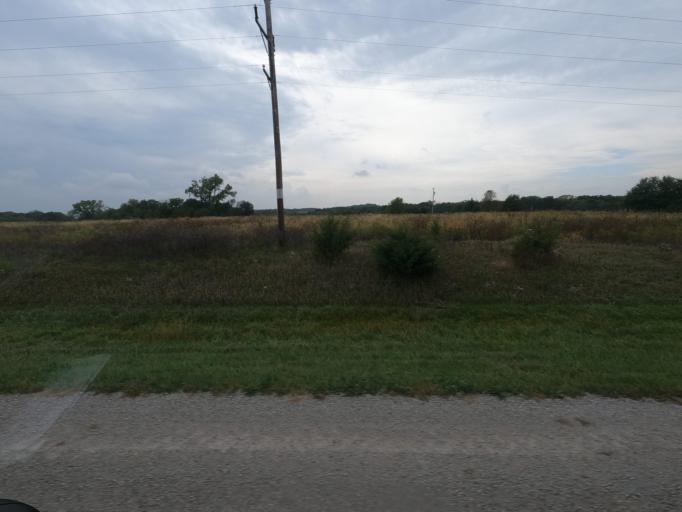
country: US
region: Iowa
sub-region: Van Buren County
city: Keosauqua
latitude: 40.8402
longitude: -92.0098
